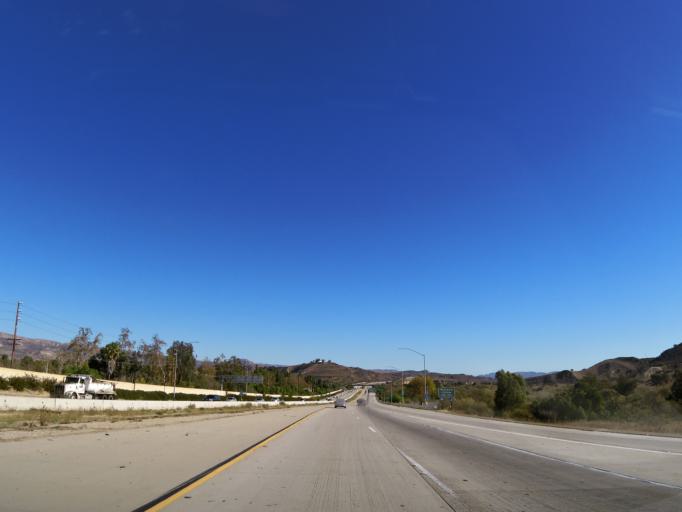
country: US
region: California
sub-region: Ventura County
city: Moorpark
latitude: 34.2929
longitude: -118.8535
